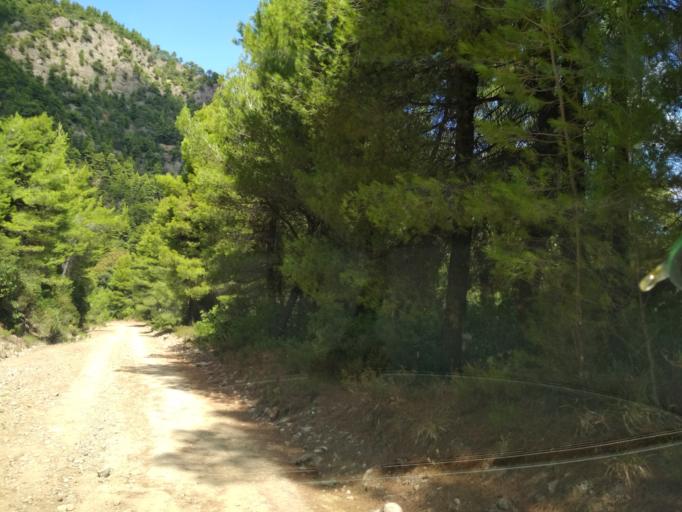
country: GR
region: Central Greece
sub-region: Nomos Evvoias
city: Roviai
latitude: 38.8421
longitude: 23.2795
